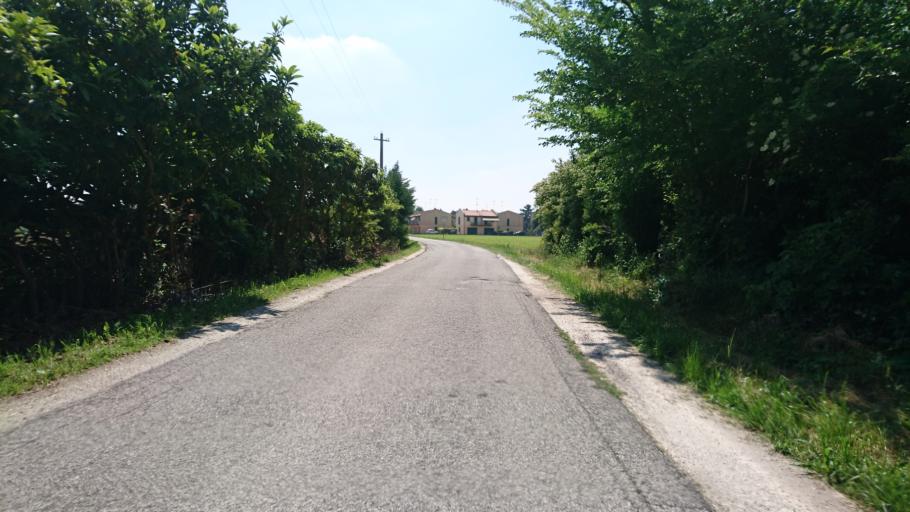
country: IT
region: Veneto
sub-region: Provincia di Padova
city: Casalserugo
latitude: 45.3011
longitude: 11.9113
